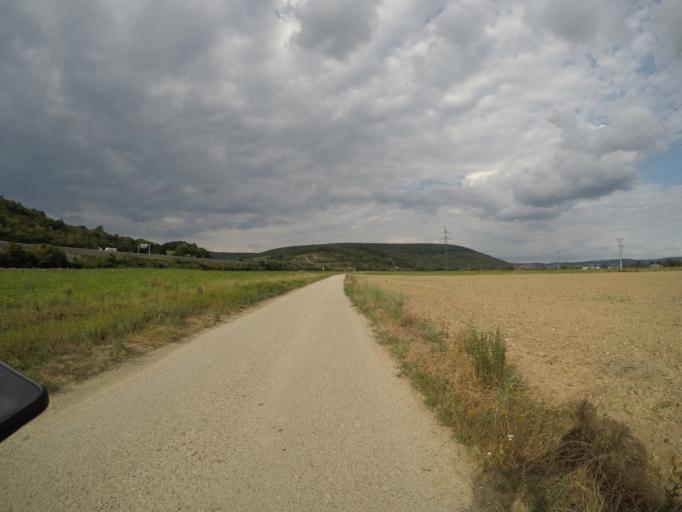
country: SK
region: Trenciansky
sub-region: Okres Trencin
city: Trencin
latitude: 48.9056
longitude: 17.9967
